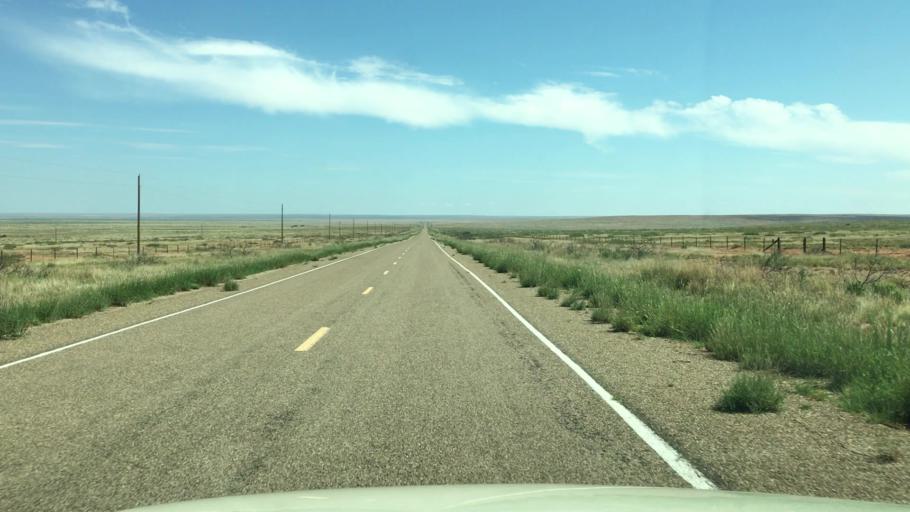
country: US
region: New Mexico
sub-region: De Baca County
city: Fort Sumner
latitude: 33.9840
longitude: -104.5734
